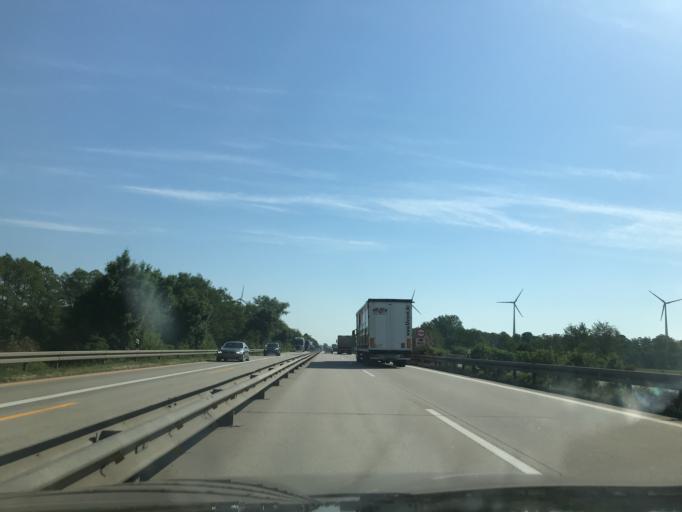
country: DE
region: Brandenburg
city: Linthe
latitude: 52.1694
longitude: 12.8078
